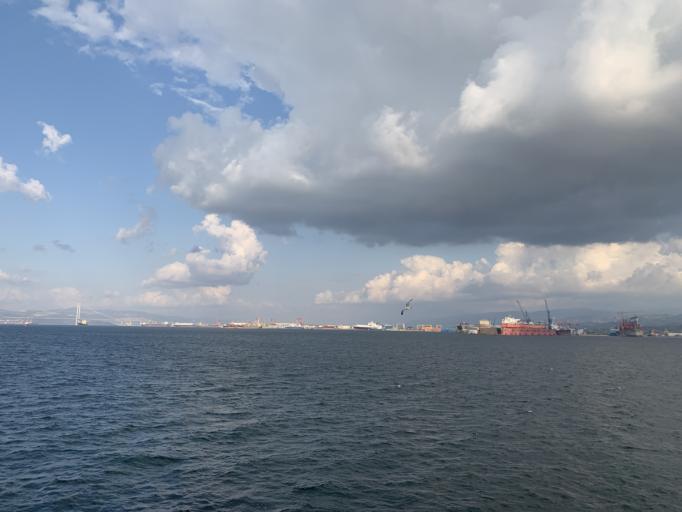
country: TR
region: Yalova
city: Altinova
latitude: 40.7169
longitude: 29.4465
